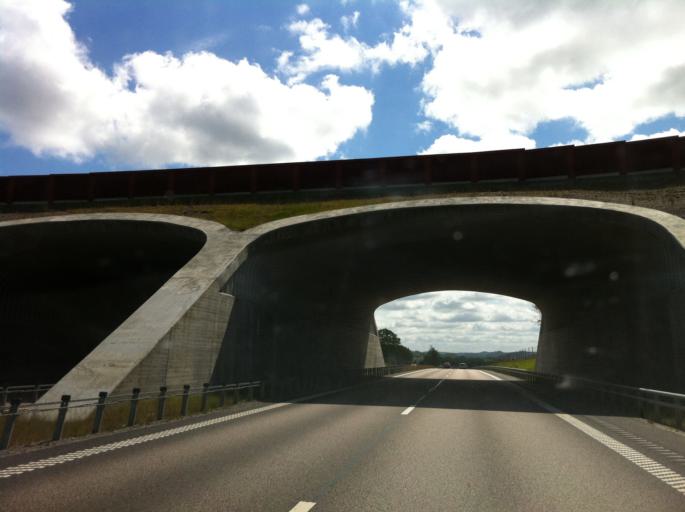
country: SE
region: Vaestra Goetaland
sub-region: Lilla Edets Kommun
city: Lilla Edet
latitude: 58.1694
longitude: 12.1385
